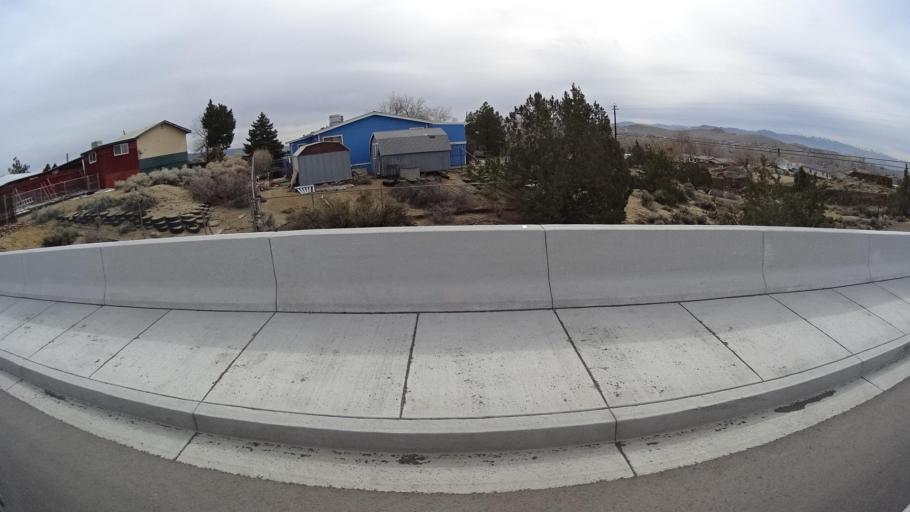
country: US
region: Nevada
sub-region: Washoe County
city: Sun Valley
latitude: 39.6078
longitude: -119.7805
